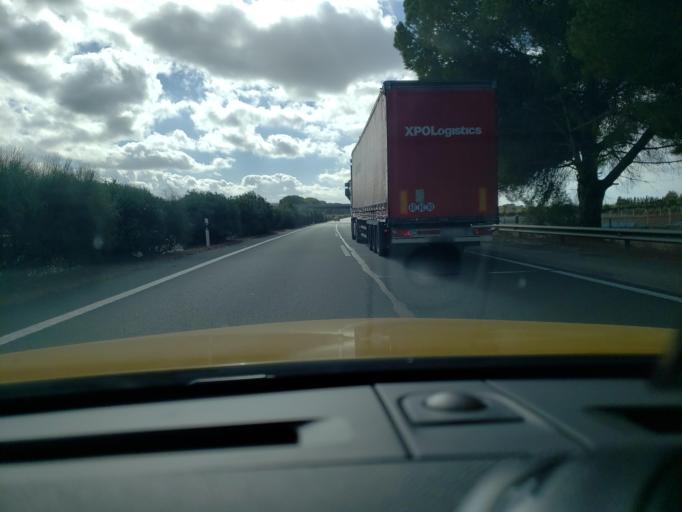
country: ES
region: Andalusia
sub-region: Provincia de Sevilla
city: Lebrija
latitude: 36.8660
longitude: -5.9942
